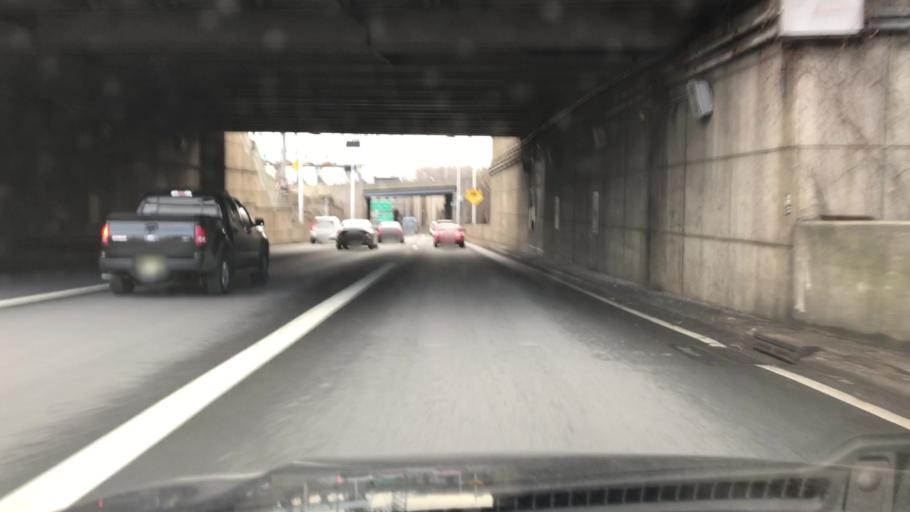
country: US
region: New Jersey
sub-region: Bergen County
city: Fort Lee
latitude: 40.8542
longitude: -73.9685
